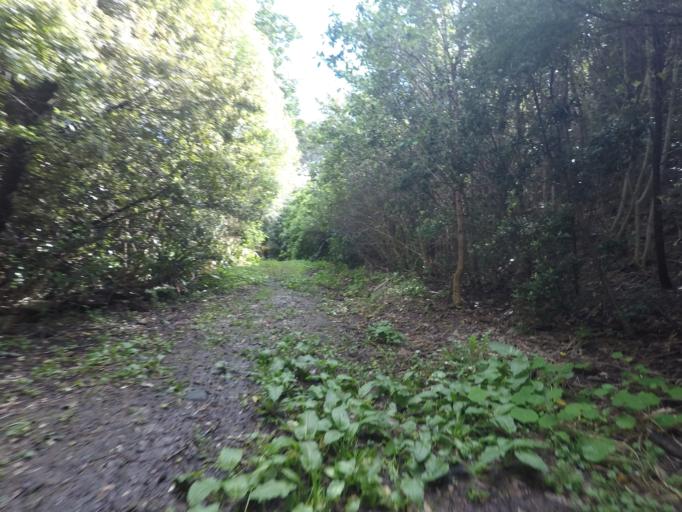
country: NZ
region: Auckland
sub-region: Auckland
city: Rosebank
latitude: -36.8803
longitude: 174.6689
